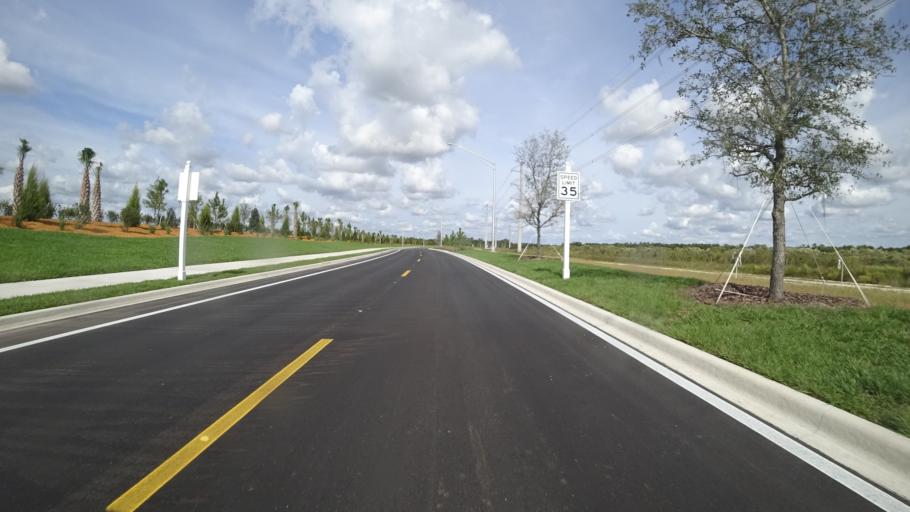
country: US
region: Florida
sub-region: Sarasota County
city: The Meadows
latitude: 27.4104
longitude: -82.3539
